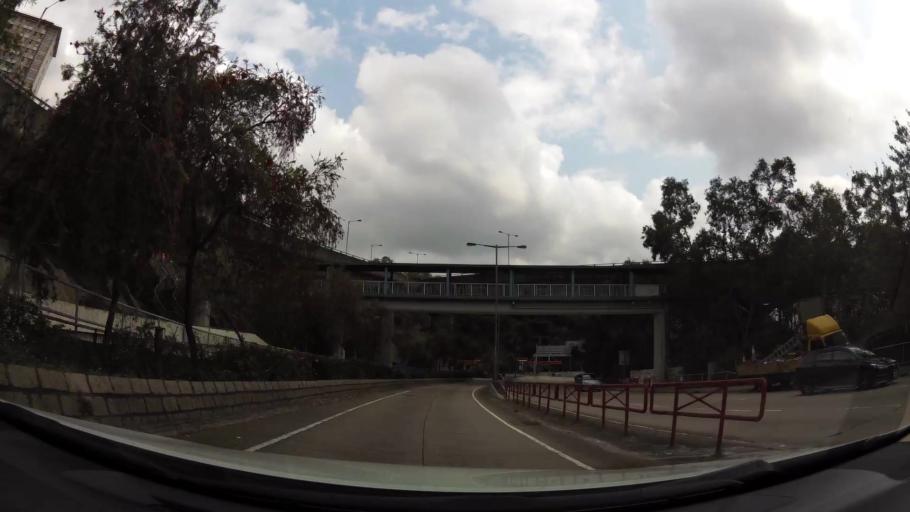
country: HK
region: Sham Shui Po
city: Sham Shui Po
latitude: 22.3399
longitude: 114.1627
